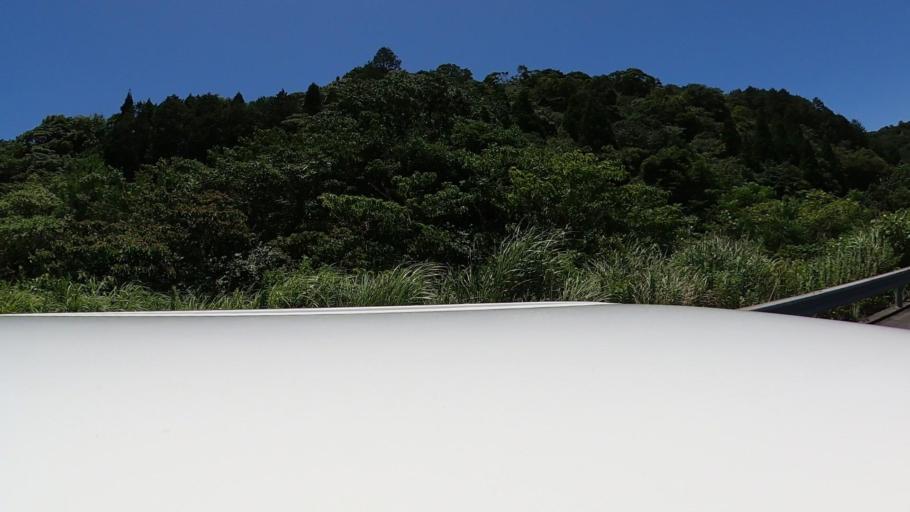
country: JP
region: Miyazaki
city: Nobeoka
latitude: 32.5386
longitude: 131.6585
